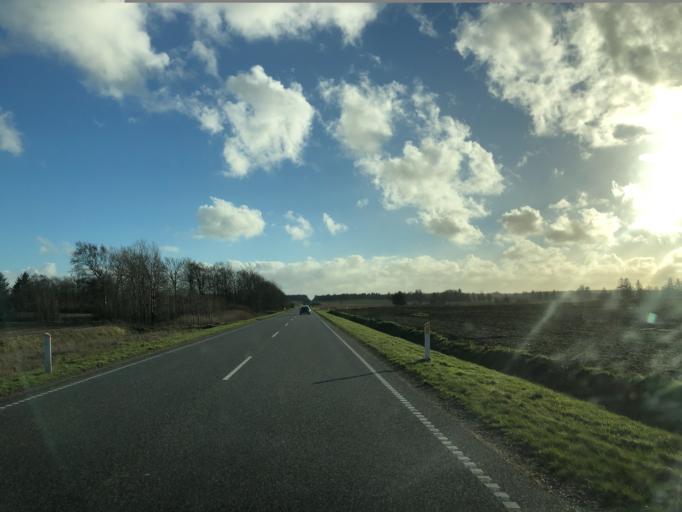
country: DK
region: Central Jutland
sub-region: Herning Kommune
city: Vildbjerg
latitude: 56.1905
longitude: 8.7105
